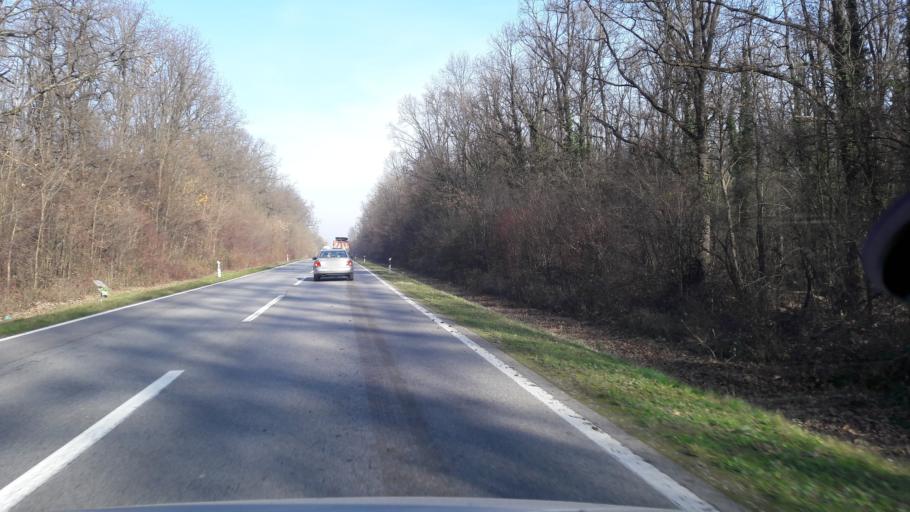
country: HR
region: Vukovarsko-Srijemska
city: Gradiste
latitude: 45.1283
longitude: 18.7159
